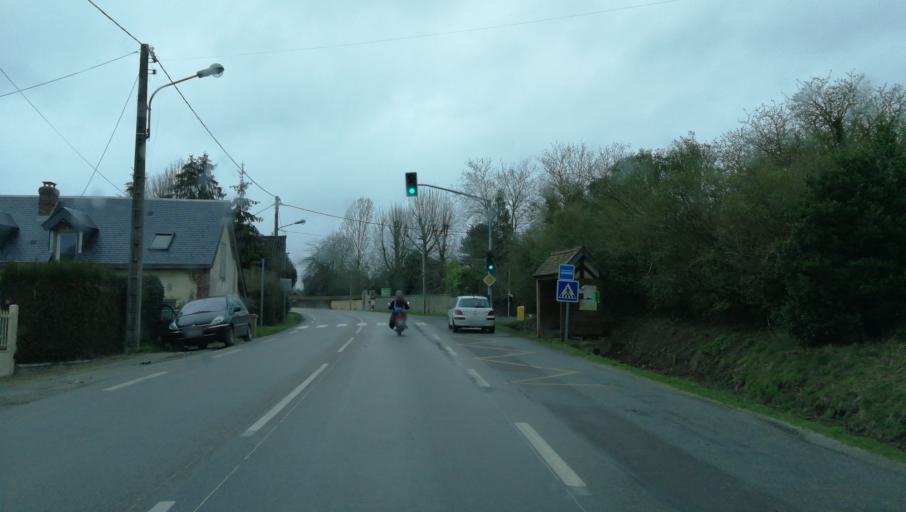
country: FR
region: Haute-Normandie
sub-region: Departement de l'Eure
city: Brionne
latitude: 49.1689
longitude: 0.7236
